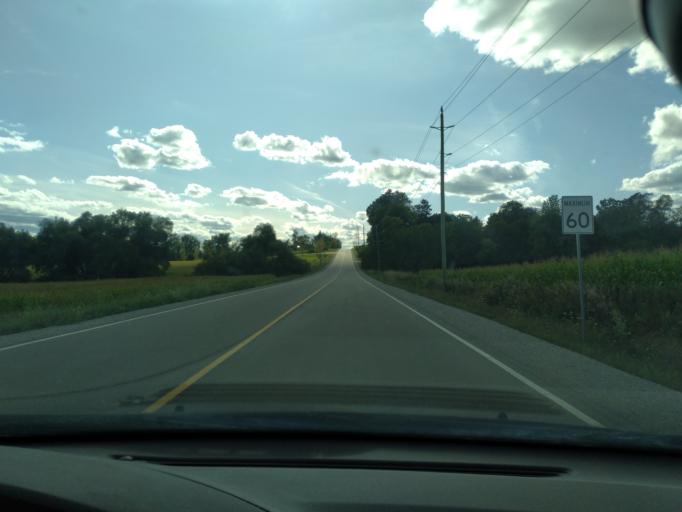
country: CA
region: Ontario
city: Bradford West Gwillimbury
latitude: 44.0821
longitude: -79.6510
